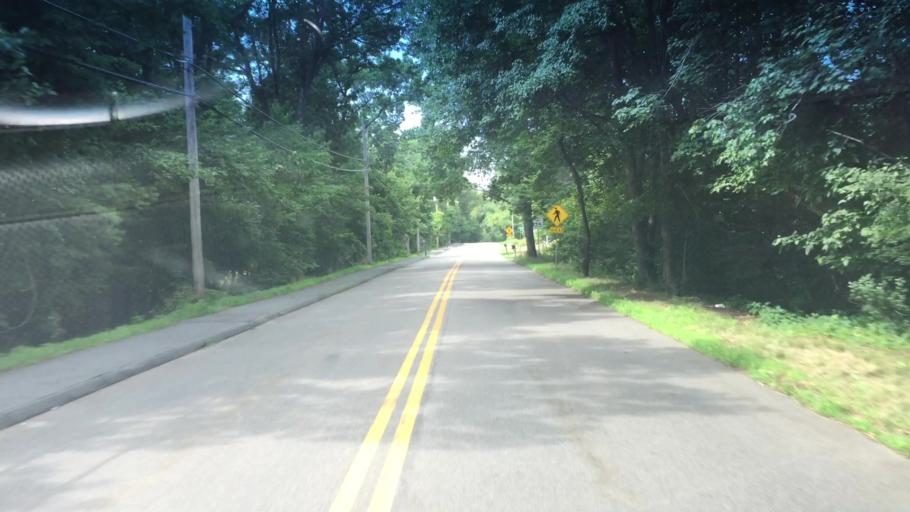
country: US
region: Massachusetts
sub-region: Norfolk County
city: Medway
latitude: 42.1215
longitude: -71.3974
